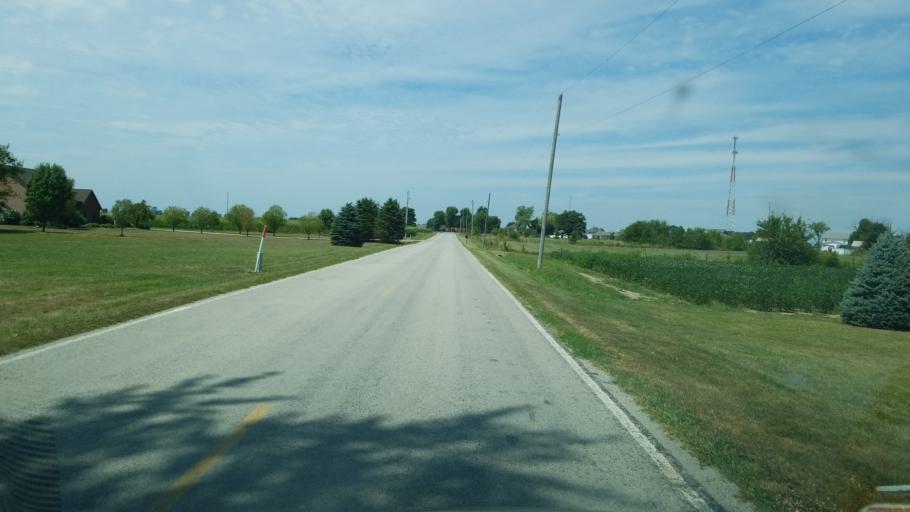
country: US
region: Ohio
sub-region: Madison County
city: West Jefferson
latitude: 40.0112
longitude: -83.3024
